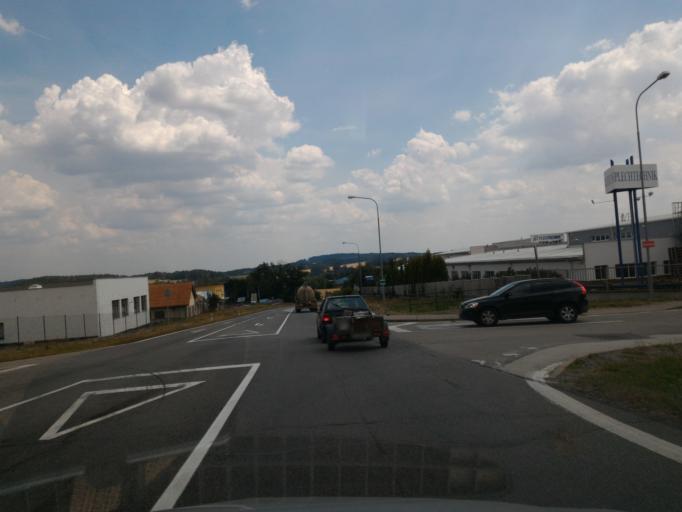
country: CZ
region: Vysocina
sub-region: Okres Havlickuv Brod
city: Havlickuv Brod
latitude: 49.6100
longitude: 15.5968
